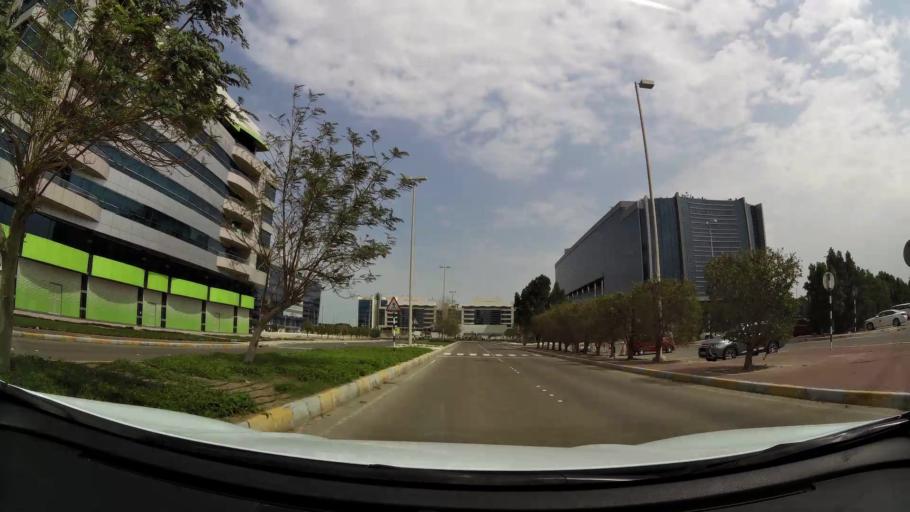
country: AE
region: Abu Dhabi
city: Abu Dhabi
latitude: 24.4280
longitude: 54.4638
